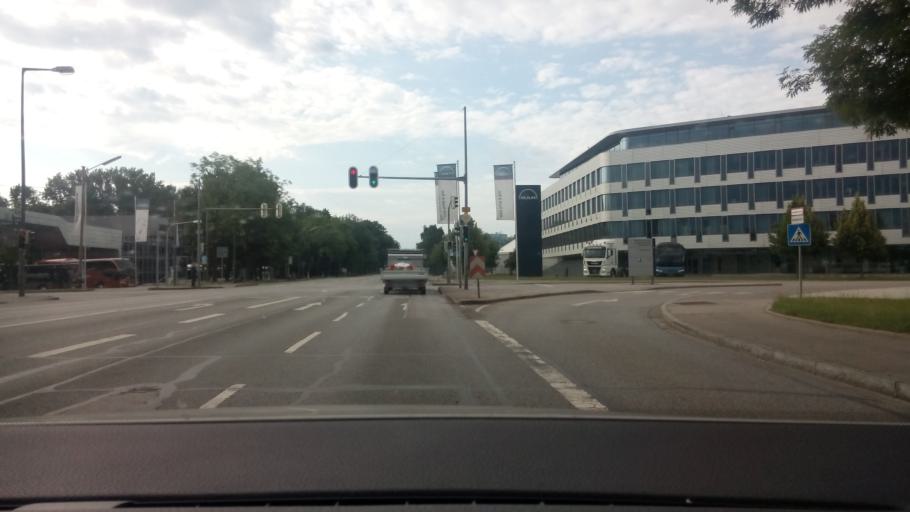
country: DE
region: Bavaria
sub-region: Upper Bavaria
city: Karlsfeld
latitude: 48.2172
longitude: 11.4796
